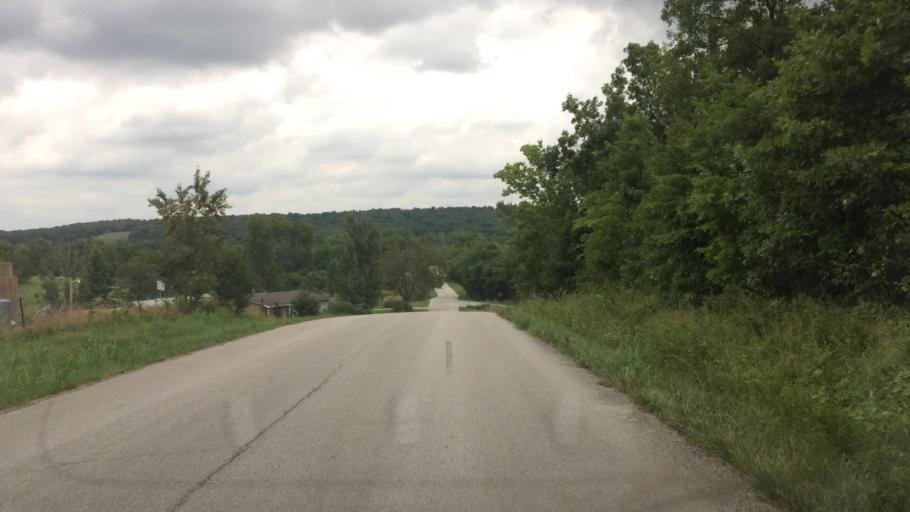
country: US
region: Missouri
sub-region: Greene County
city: Strafford
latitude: 37.3220
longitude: -93.0578
